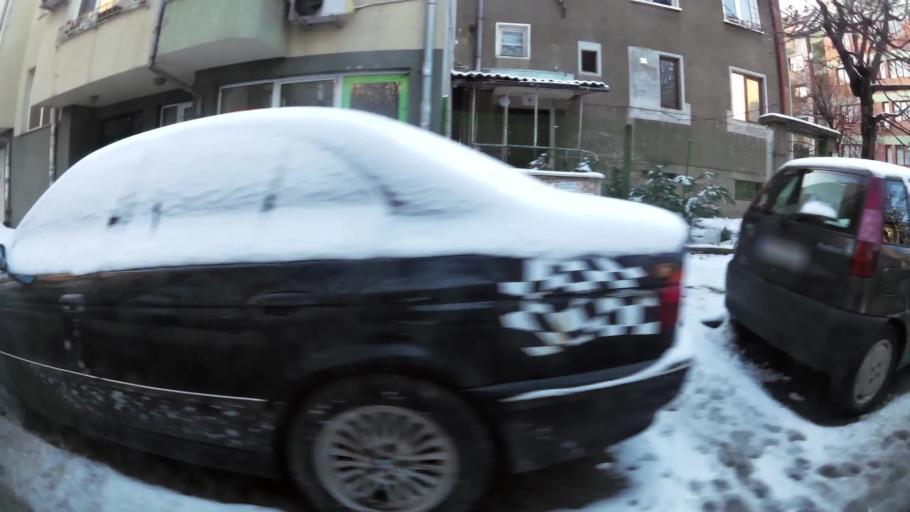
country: BG
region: Sofia-Capital
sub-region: Stolichna Obshtina
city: Sofia
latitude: 42.6893
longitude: 23.3655
